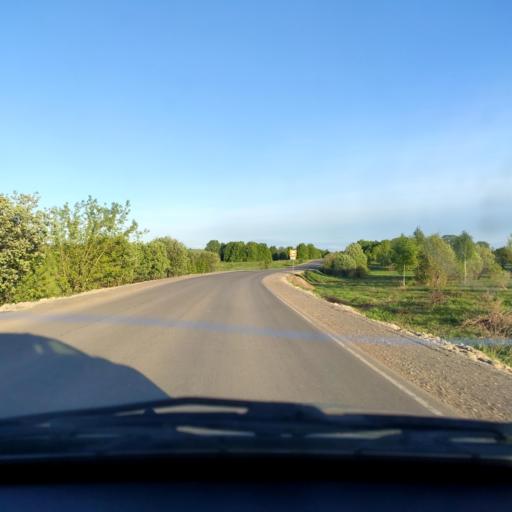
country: RU
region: Bashkortostan
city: Yazykovo
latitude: 55.0352
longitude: 56.1986
